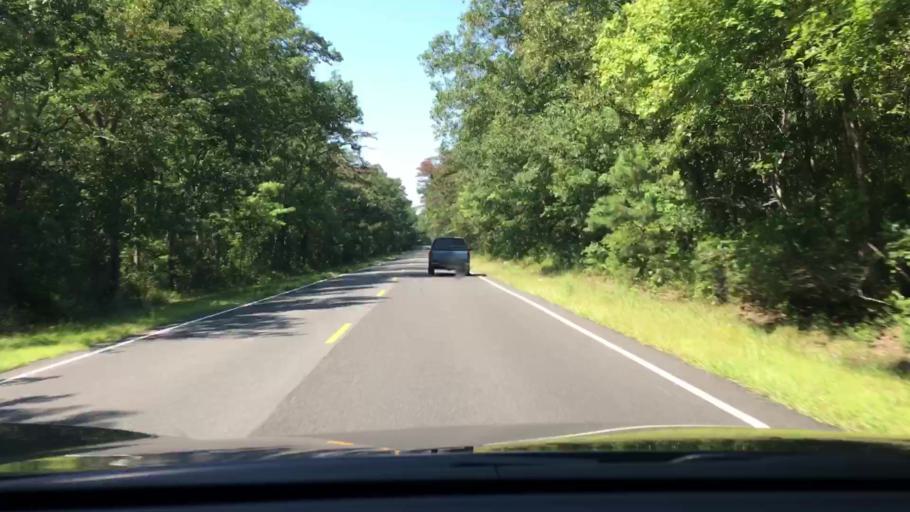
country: US
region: New Jersey
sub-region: Cape May County
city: Woodbine
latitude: 39.2606
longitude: -74.9212
